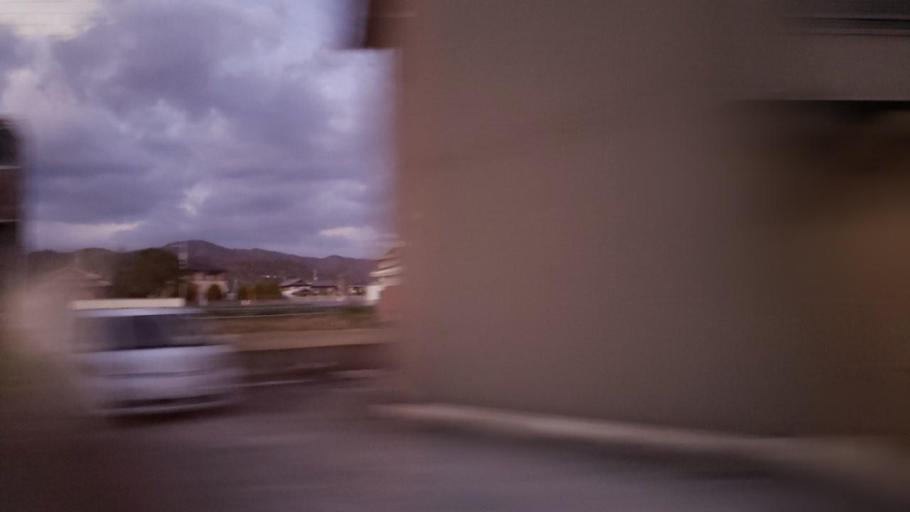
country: JP
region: Tokushima
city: Kamojimacho-jogejima
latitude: 34.0896
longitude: 134.2876
